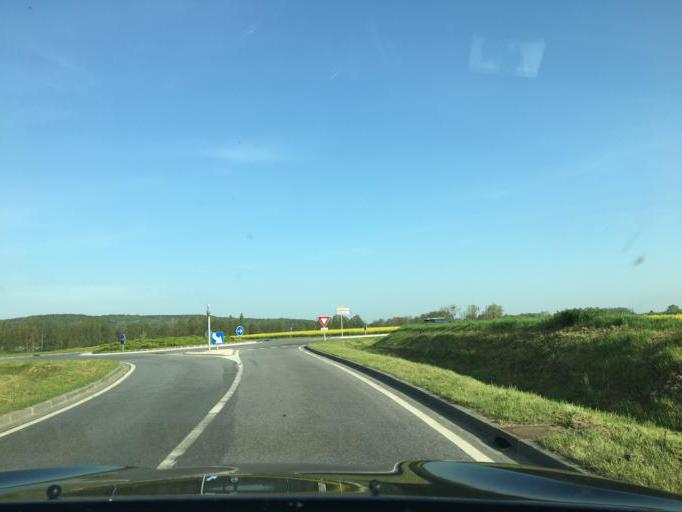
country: FR
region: Ile-de-France
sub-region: Departement des Yvelines
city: Conde-sur-Vesgre
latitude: 48.7475
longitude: 1.6643
